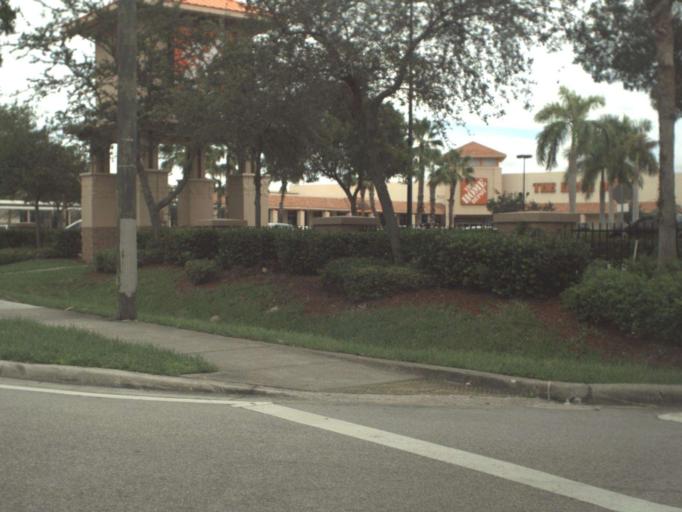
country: US
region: Florida
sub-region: Miami-Dade County
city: Biscayne Park
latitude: 25.8864
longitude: -80.1646
